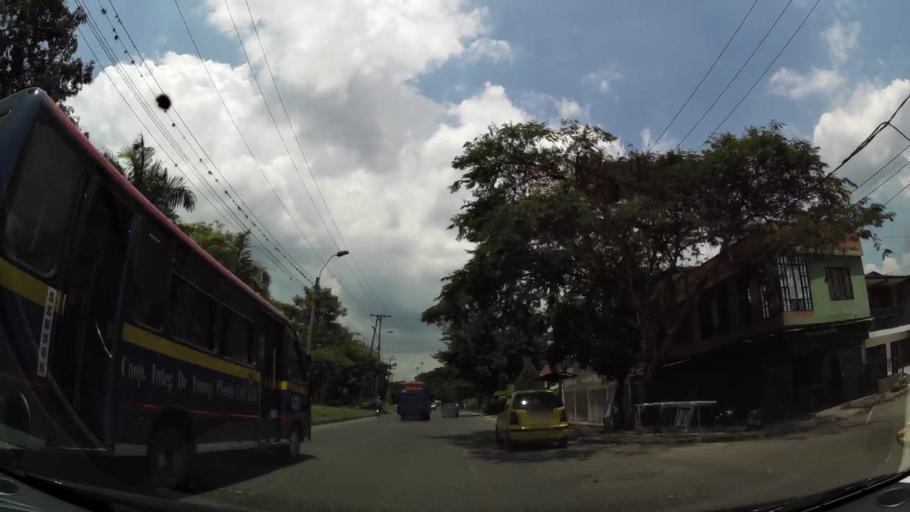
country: CO
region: Valle del Cauca
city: Cali
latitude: 3.4490
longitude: -76.4831
